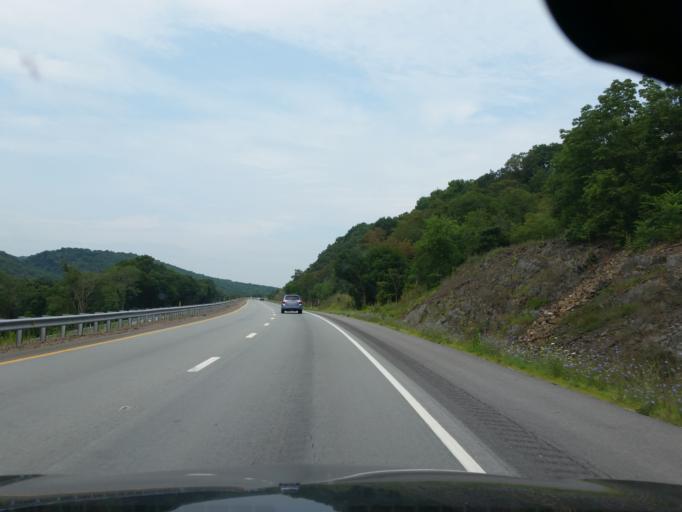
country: US
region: Pennsylvania
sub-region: Perry County
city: Newport
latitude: 40.4808
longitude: -77.0545
